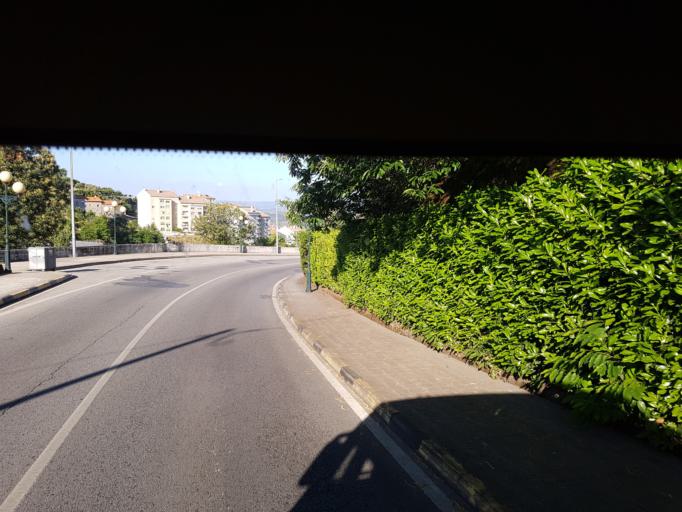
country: PT
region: Castelo Branco
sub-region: Covilha
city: Covilha
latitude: 40.2761
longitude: -7.5071
